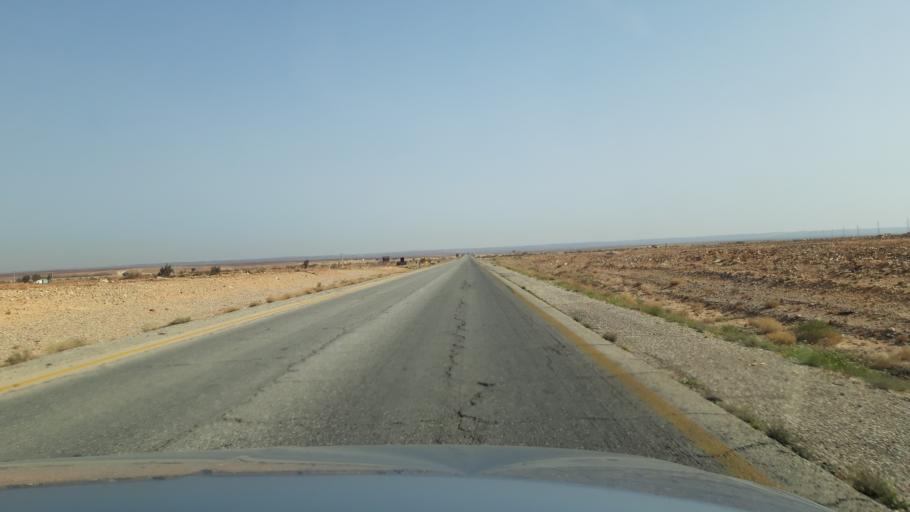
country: JO
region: Amman
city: Al Azraq ash Shamali
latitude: 31.7917
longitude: 36.5832
